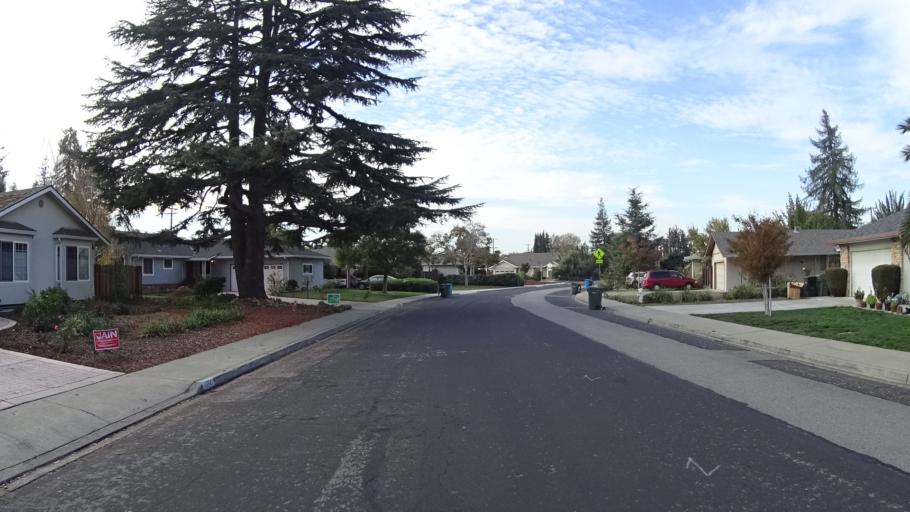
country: US
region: California
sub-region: Santa Clara County
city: Santa Clara
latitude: 37.3372
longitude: -121.9593
